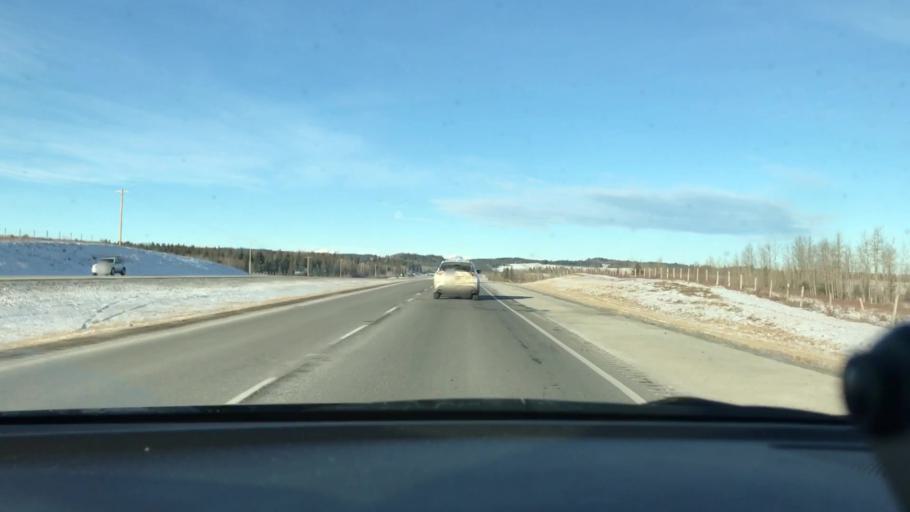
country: CA
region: Alberta
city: Cochrane
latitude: 51.1218
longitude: -114.6703
